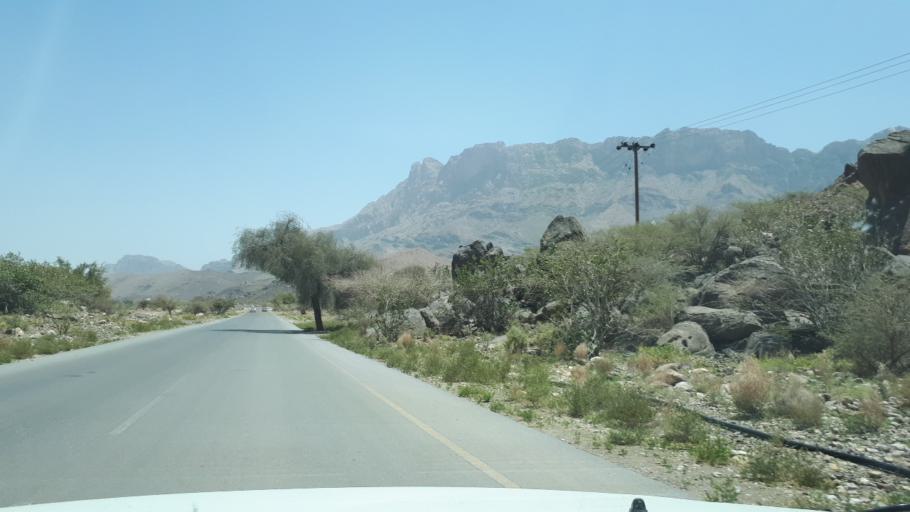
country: OM
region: Muhafazat ad Dakhiliyah
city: Bahla'
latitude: 23.1678
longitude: 57.1579
